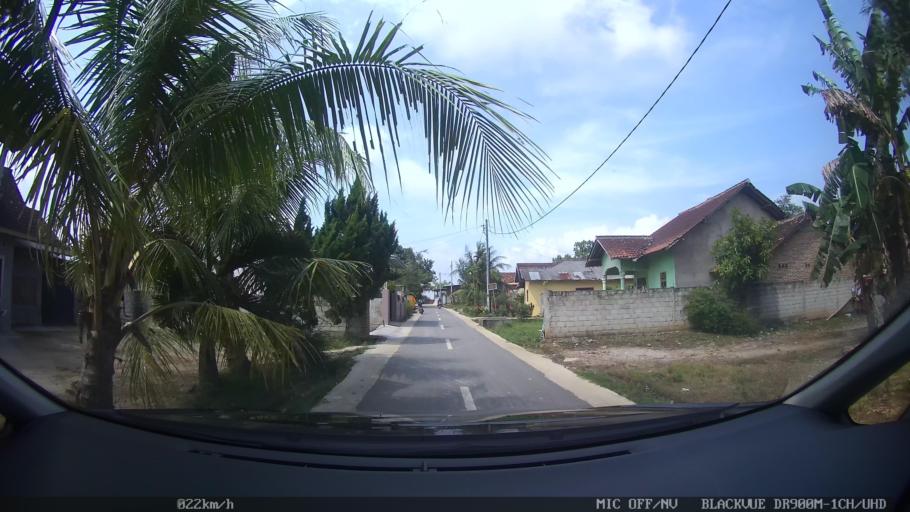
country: ID
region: Lampung
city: Kedaton
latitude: -5.3395
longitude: 105.2718
